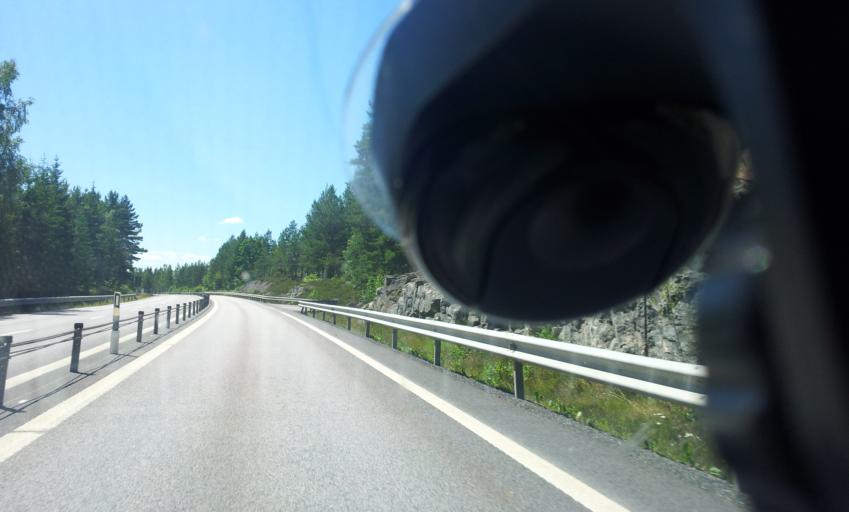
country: SE
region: OEstergoetland
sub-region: Valdemarsviks Kommun
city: Valdemarsvik
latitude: 58.0952
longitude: 16.5286
